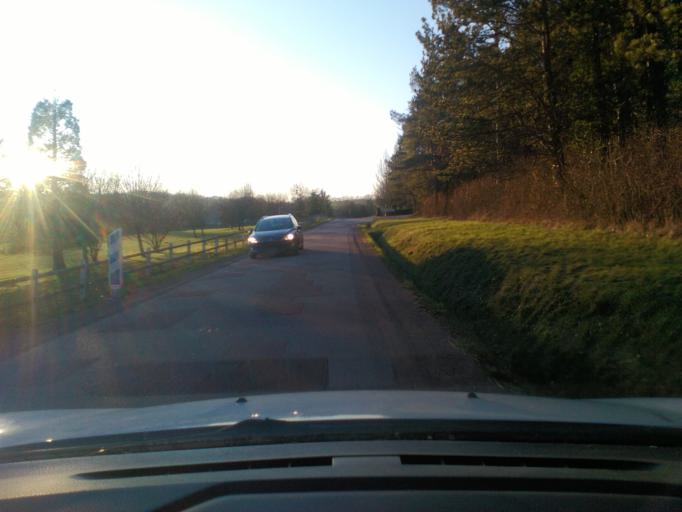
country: FR
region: Lorraine
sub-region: Departement des Vosges
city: Mirecourt
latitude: 48.2975
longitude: 6.1091
